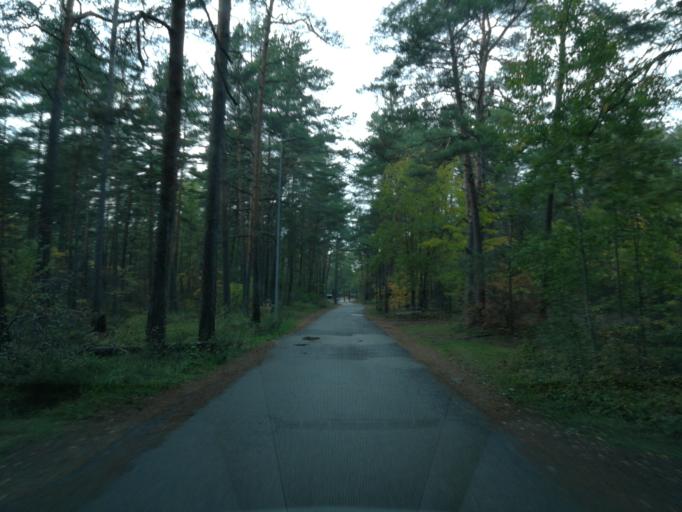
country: LV
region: Riga
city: Jaunciems
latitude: 57.0843
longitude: 24.1551
